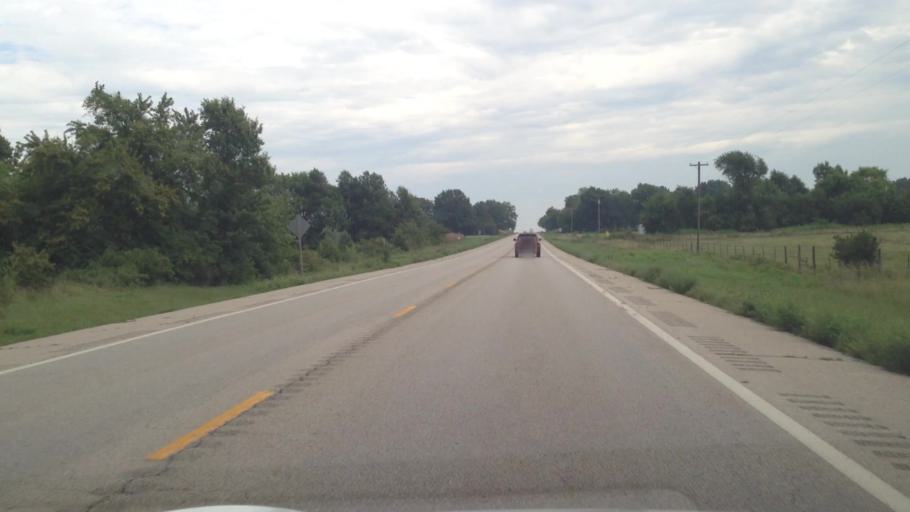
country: US
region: Kansas
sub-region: Crawford County
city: Pittsburg
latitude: 37.3393
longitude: -94.8121
